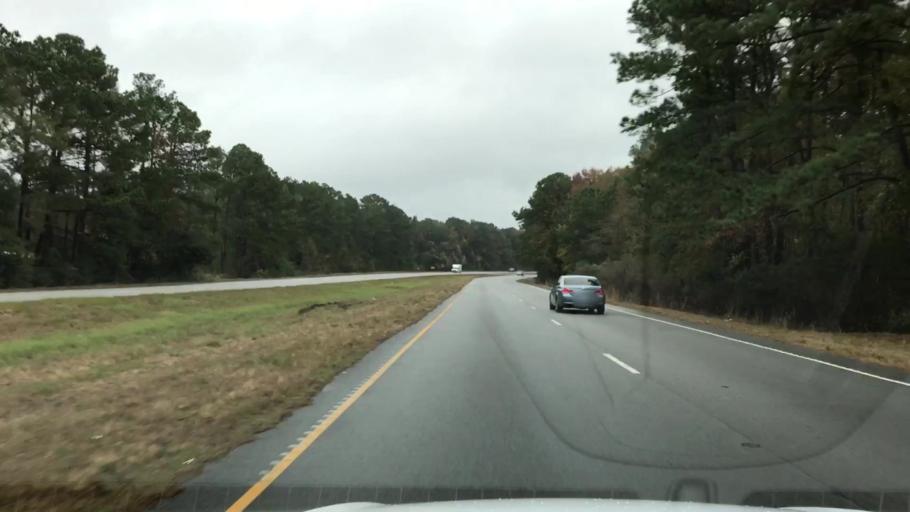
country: US
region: South Carolina
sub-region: Charleston County
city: Awendaw
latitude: 32.9340
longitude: -79.7125
